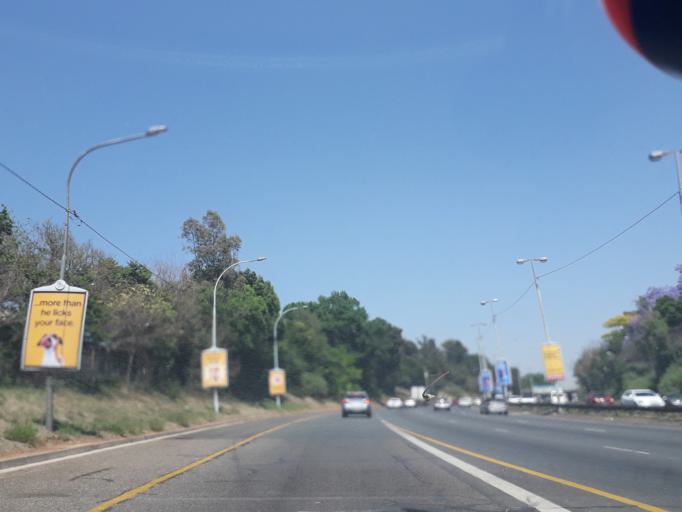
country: ZA
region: Gauteng
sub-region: City of Johannesburg Metropolitan Municipality
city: Johannesburg
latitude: -26.1692
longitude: 28.0528
